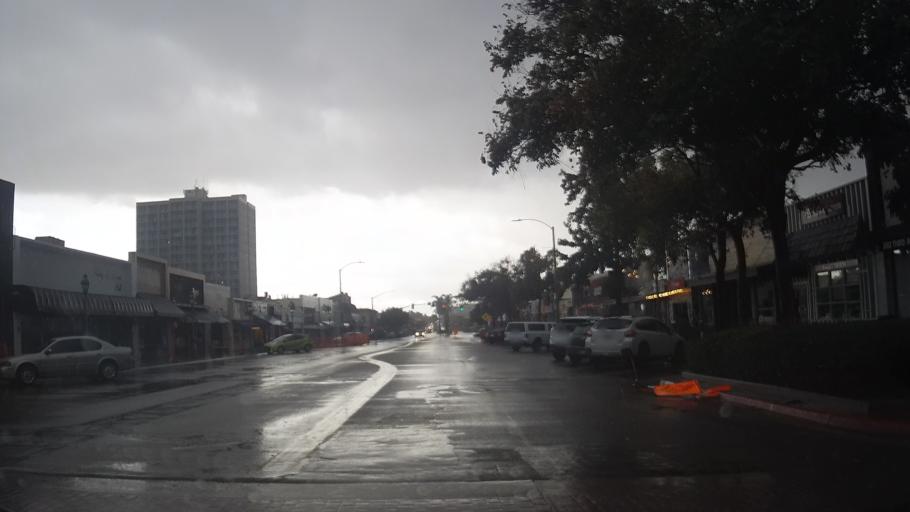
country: US
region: California
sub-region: San Diego County
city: Chula Vista
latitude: 32.6430
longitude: -117.0806
